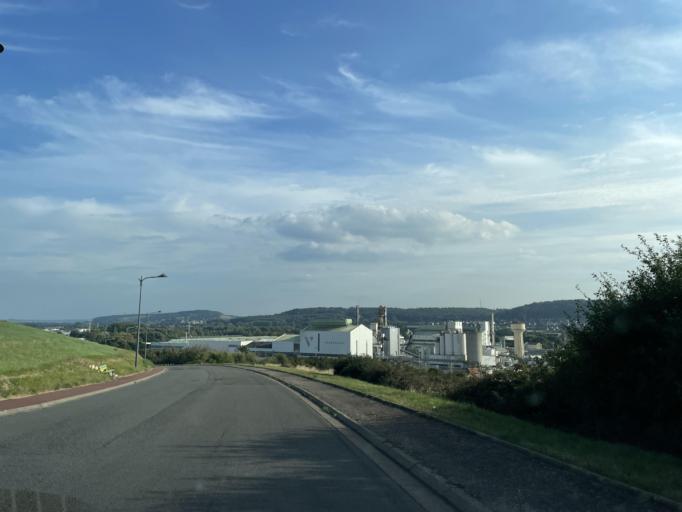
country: FR
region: Picardie
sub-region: Departement de la Somme
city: Mers-les-Bains
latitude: 50.0666
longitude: 1.3932
